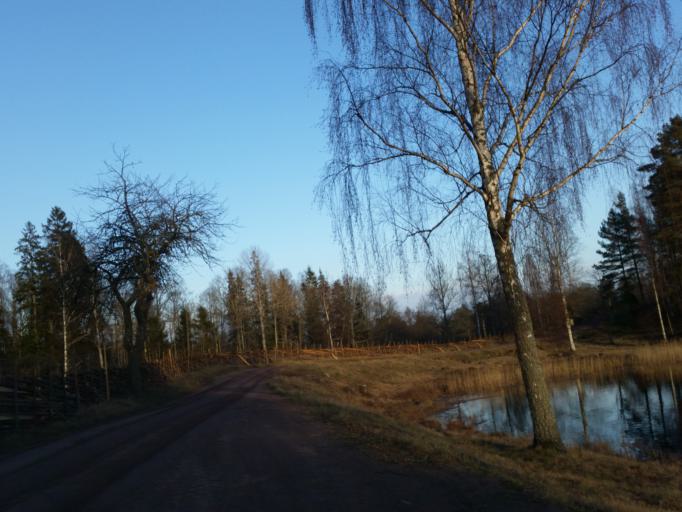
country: SE
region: Kalmar
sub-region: Oskarshamns Kommun
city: Oskarshamn
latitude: 57.3389
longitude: 16.4719
